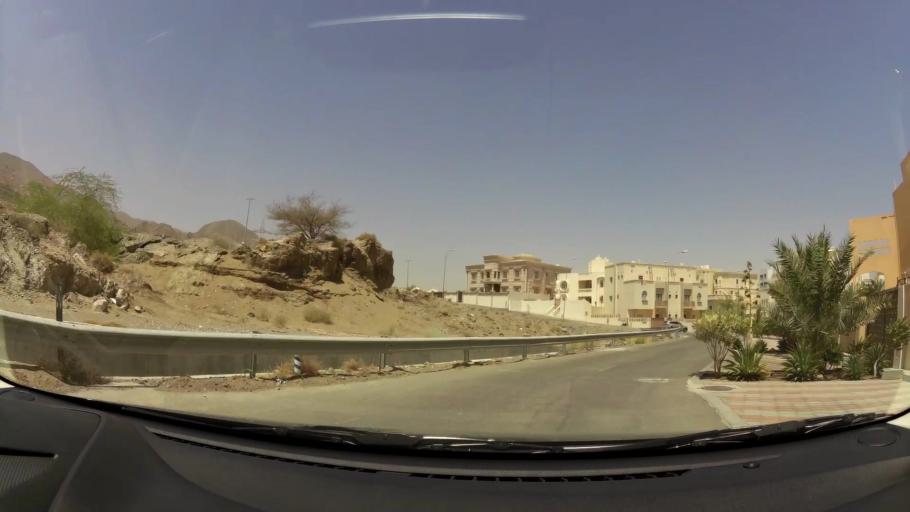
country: OM
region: Muhafazat Masqat
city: Bawshar
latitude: 23.5848
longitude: 58.4520
